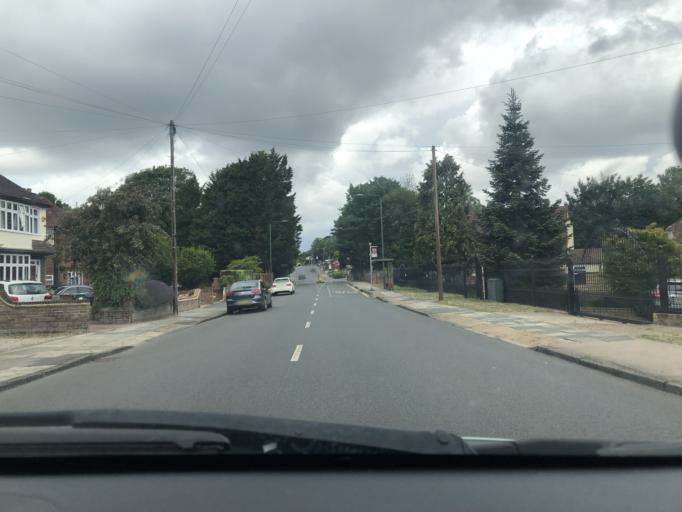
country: GB
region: England
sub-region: Greater London
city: Bexley
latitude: 51.4443
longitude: 0.1366
